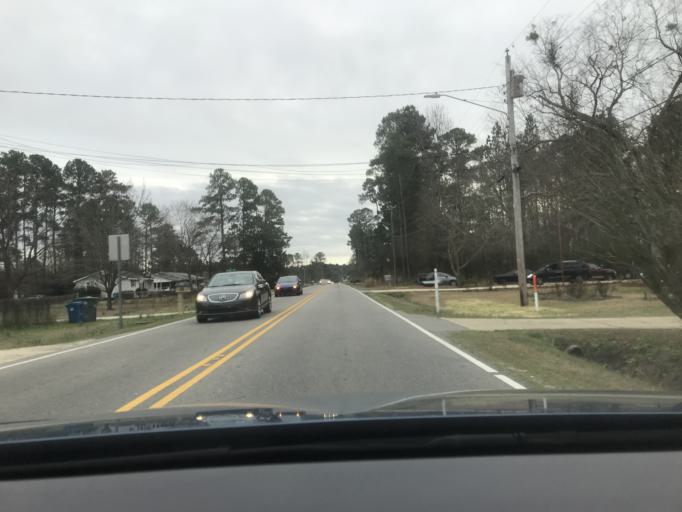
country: US
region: North Carolina
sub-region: Cumberland County
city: Fort Bragg
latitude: 35.0578
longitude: -79.0121
